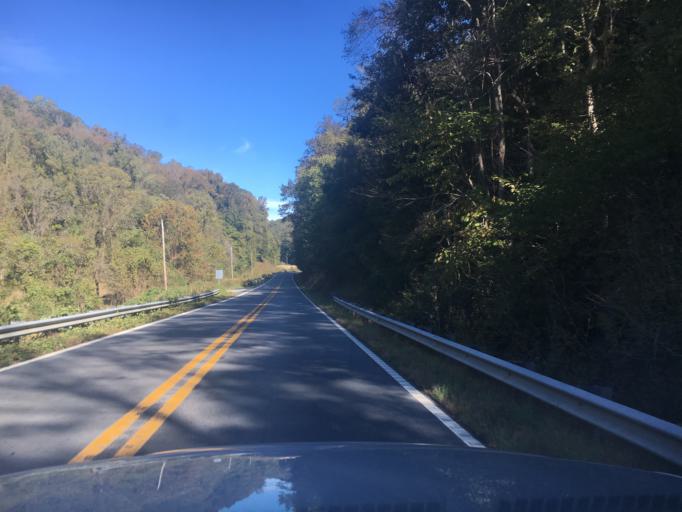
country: US
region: North Carolina
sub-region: Burke County
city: Glen Alpine
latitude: 35.5650
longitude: -81.8513
